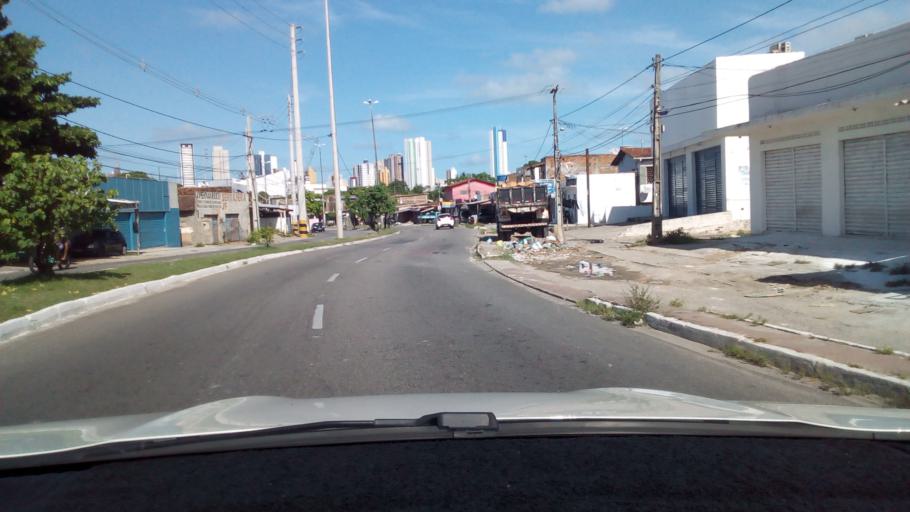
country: BR
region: Paraiba
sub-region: Joao Pessoa
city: Joao Pessoa
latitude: -7.0986
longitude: -34.8528
